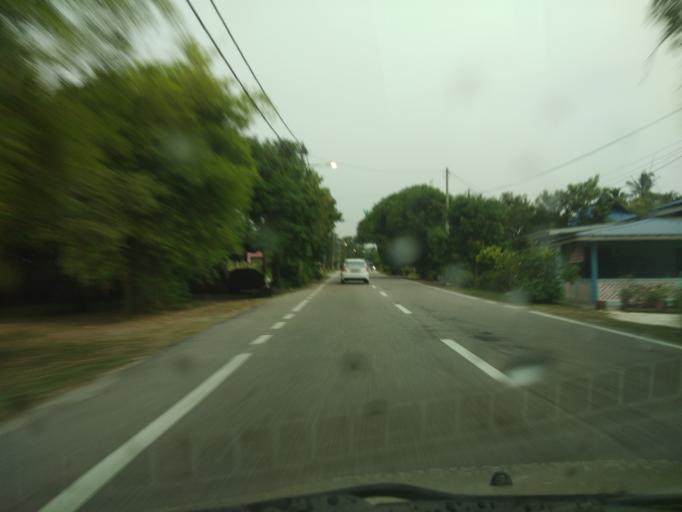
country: MY
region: Penang
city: Permatang Kuching
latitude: 5.4836
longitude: 100.4009
